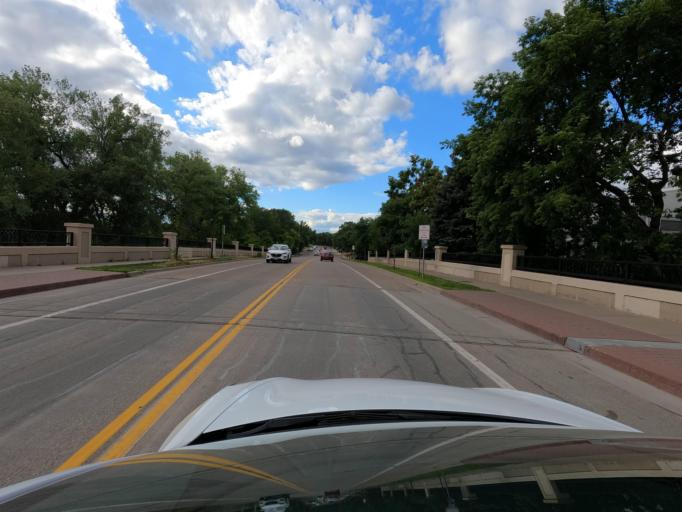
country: US
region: Minnesota
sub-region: Hennepin County
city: Minneapolis
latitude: 44.9891
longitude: -93.2607
